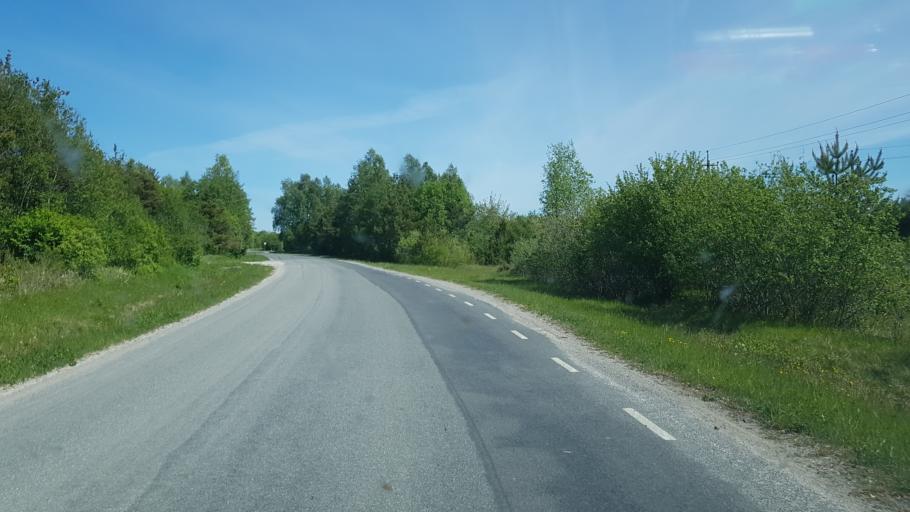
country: EE
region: Saare
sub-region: Kuressaare linn
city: Kuressaare
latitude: 58.2760
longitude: 22.5002
